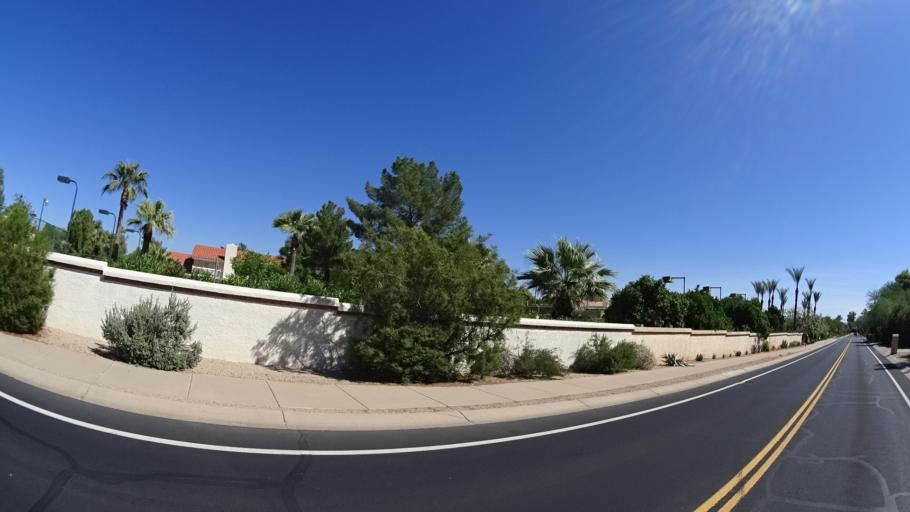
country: US
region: Arizona
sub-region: Maricopa County
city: Paradise Valley
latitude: 33.5459
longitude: -111.9317
